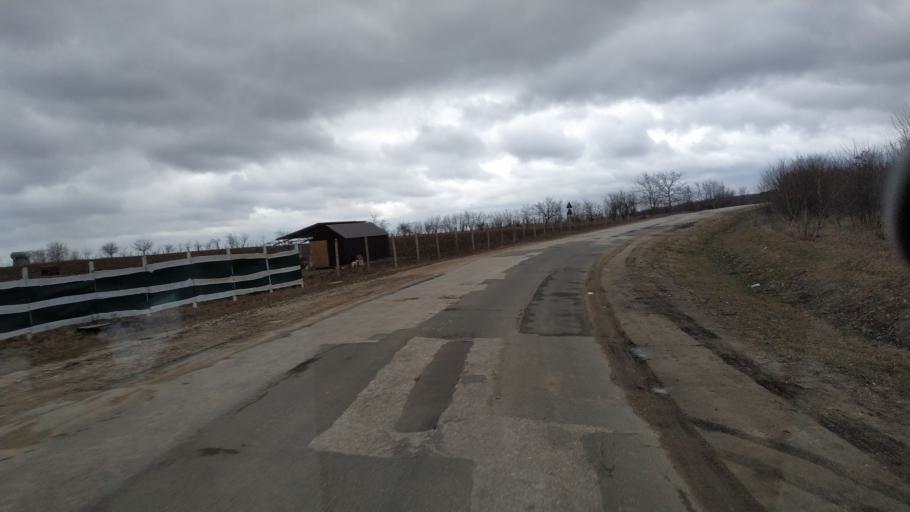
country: MD
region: Calarasi
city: Calarasi
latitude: 47.2209
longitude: 28.2723
